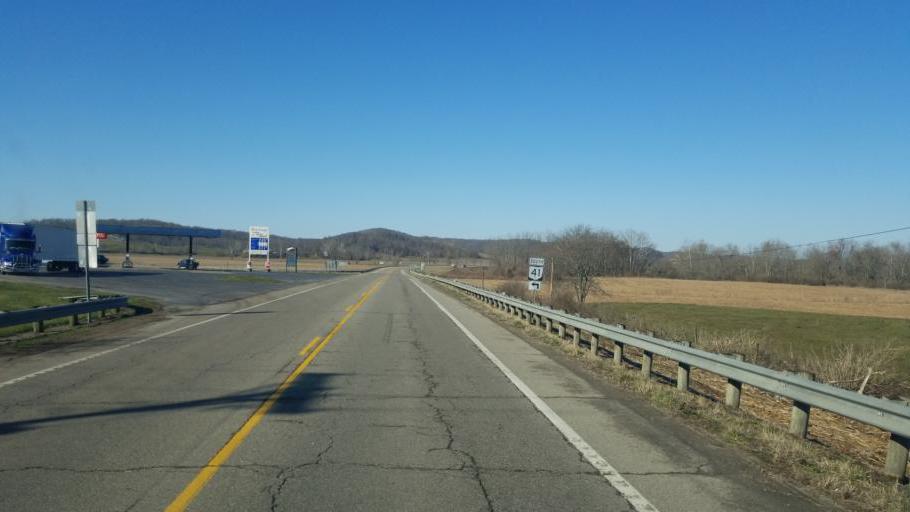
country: US
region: Ohio
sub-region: Highland County
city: Greenfield
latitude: 39.2228
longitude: -83.2834
